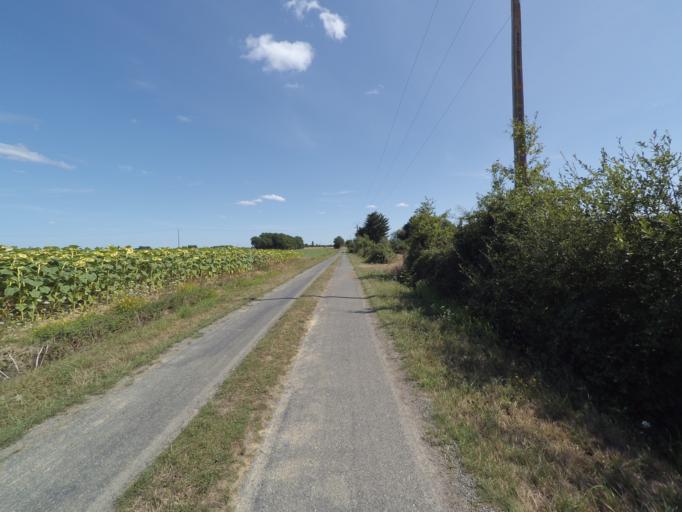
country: FR
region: Pays de la Loire
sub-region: Departement de la Loire-Atlantique
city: Vieillevigne
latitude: 46.9636
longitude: -1.4153
